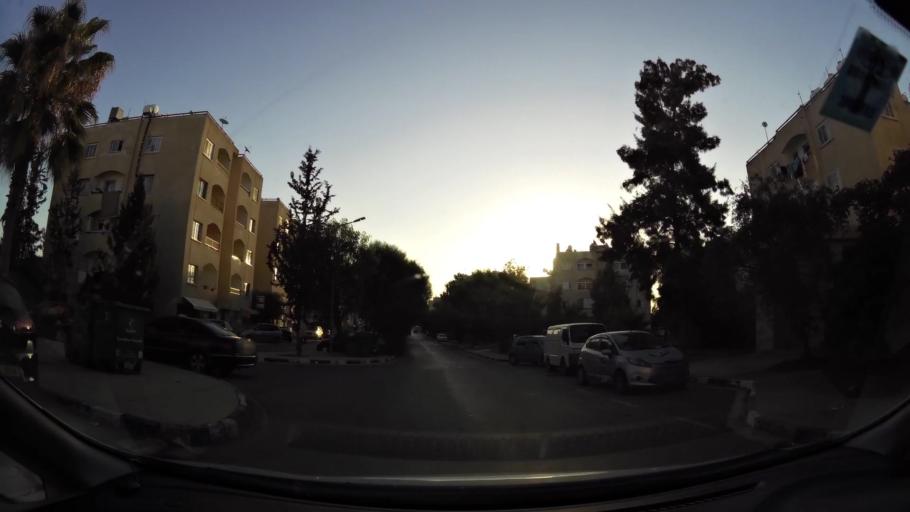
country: CY
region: Lefkosia
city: Nicosia
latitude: 35.1888
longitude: 33.3222
